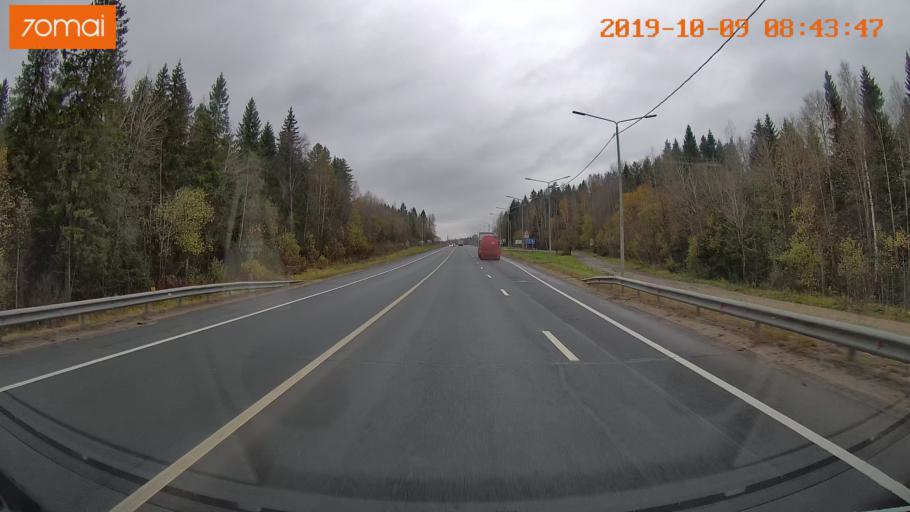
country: RU
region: Vologda
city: Gryazovets
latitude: 59.0276
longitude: 40.1126
